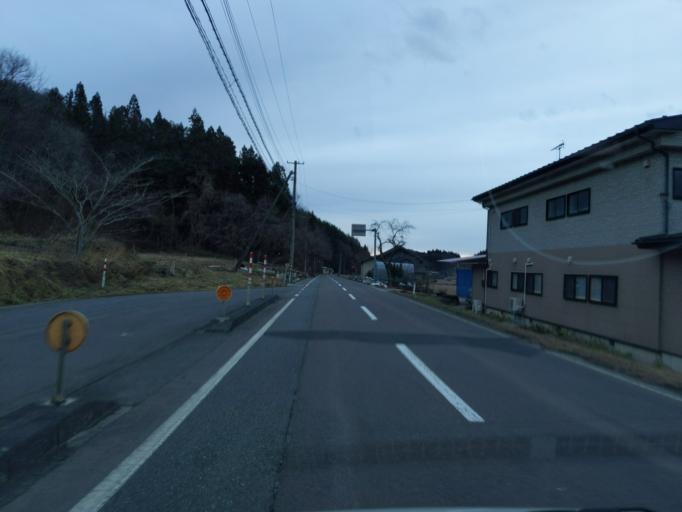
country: JP
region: Iwate
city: Mizusawa
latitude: 39.0565
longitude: 141.2892
